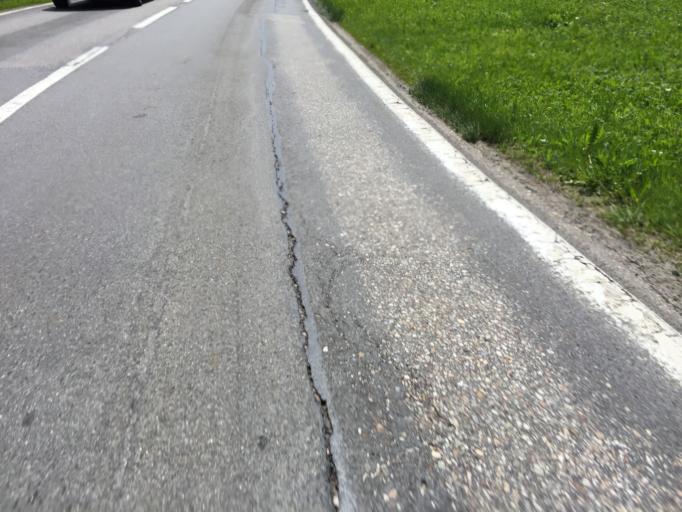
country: CH
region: Bern
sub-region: Emmental District
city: Trub
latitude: 46.9050
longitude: 7.8871
